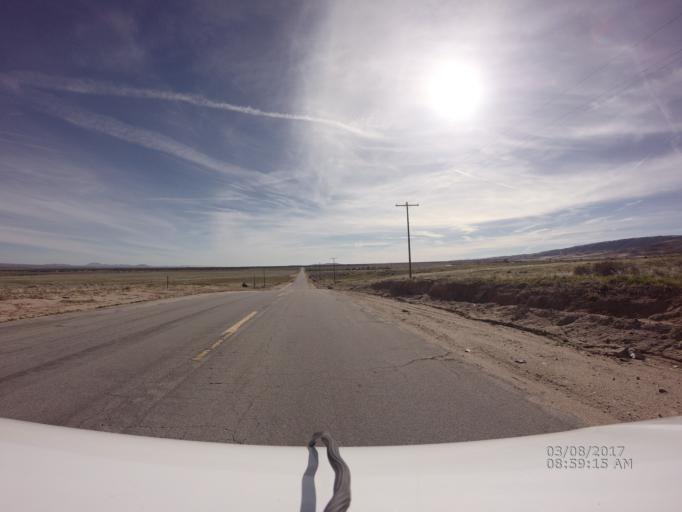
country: US
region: California
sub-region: Los Angeles County
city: Green Valley
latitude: 34.7610
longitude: -118.5308
